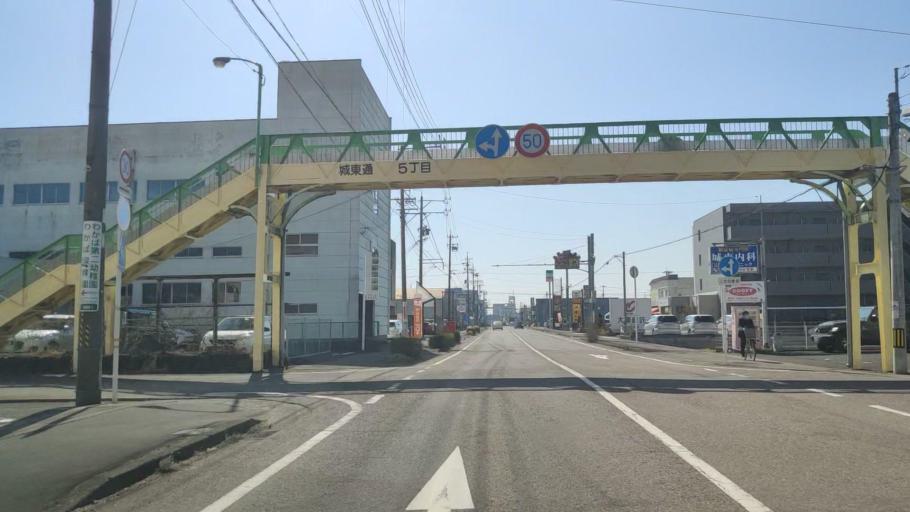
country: JP
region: Gifu
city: Kasamatsucho
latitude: 35.3941
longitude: 136.7649
